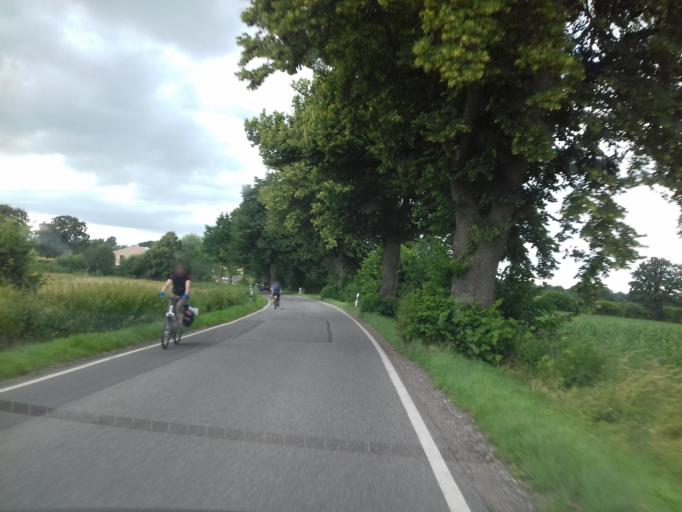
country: DE
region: Schleswig-Holstein
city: Elmenhorst
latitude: 53.7726
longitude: 10.2534
